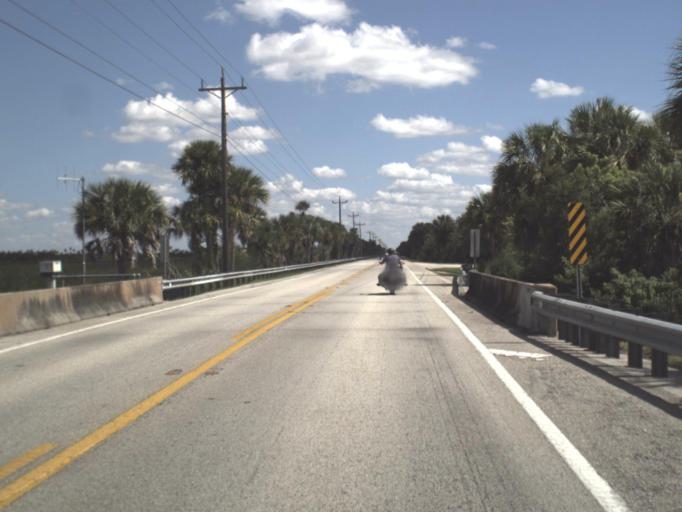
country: US
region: Florida
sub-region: Collier County
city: Marco
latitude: 25.9336
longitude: -81.4483
